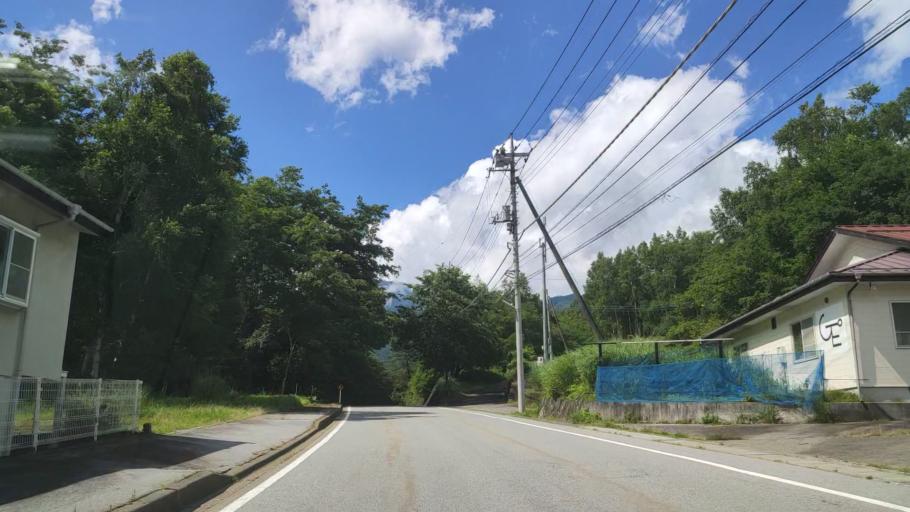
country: JP
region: Yamanashi
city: Enzan
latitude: 35.8514
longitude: 138.7591
